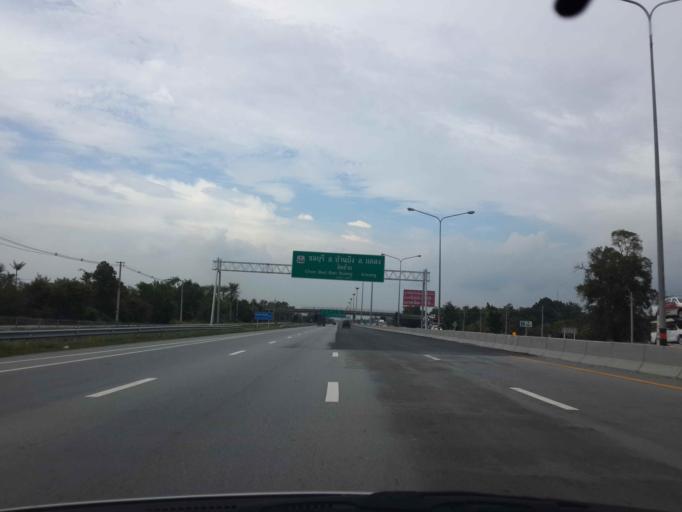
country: TH
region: Chon Buri
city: Chon Buri
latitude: 13.3294
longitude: 101.0183
